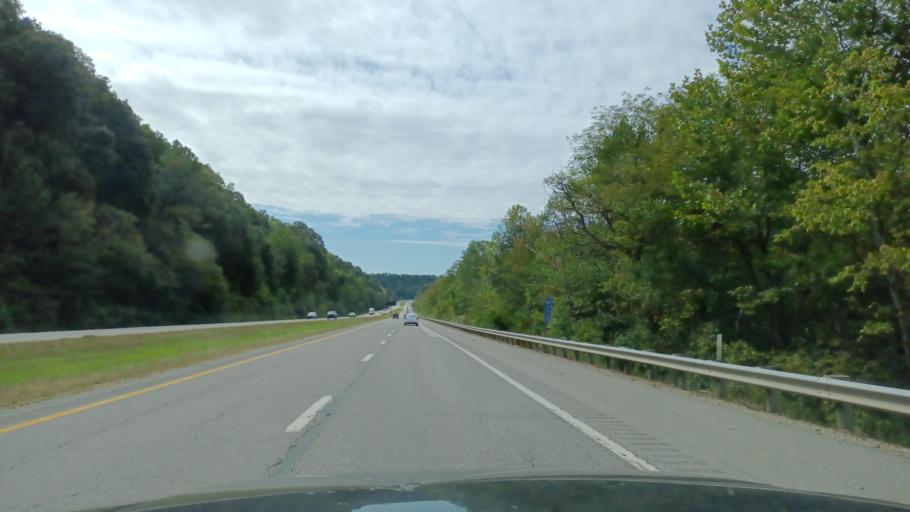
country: US
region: Ohio
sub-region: Washington County
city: Reno
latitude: 39.2469
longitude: -81.3869
